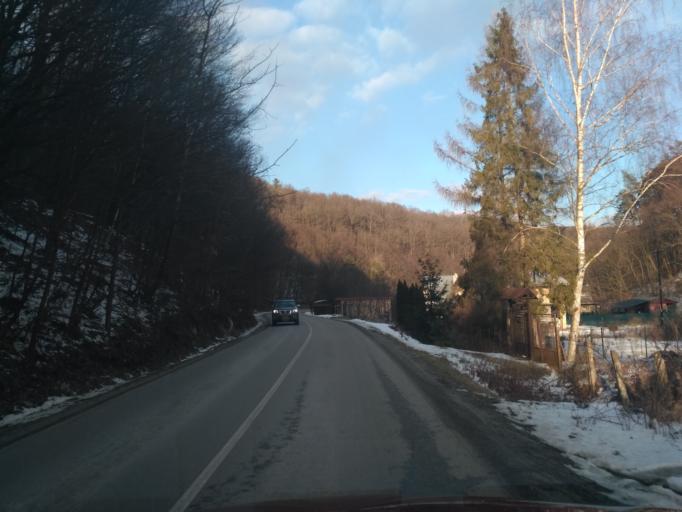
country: SK
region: Kosicky
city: Kosice
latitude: 48.7237
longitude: 21.1719
